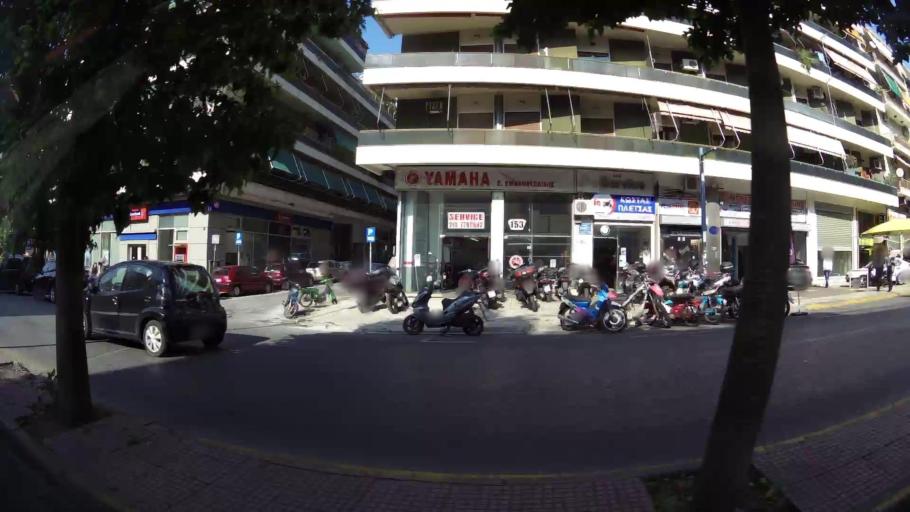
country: GR
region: Attica
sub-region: Nomarchia Athinas
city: Kaisariani
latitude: 37.9837
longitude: 23.7633
